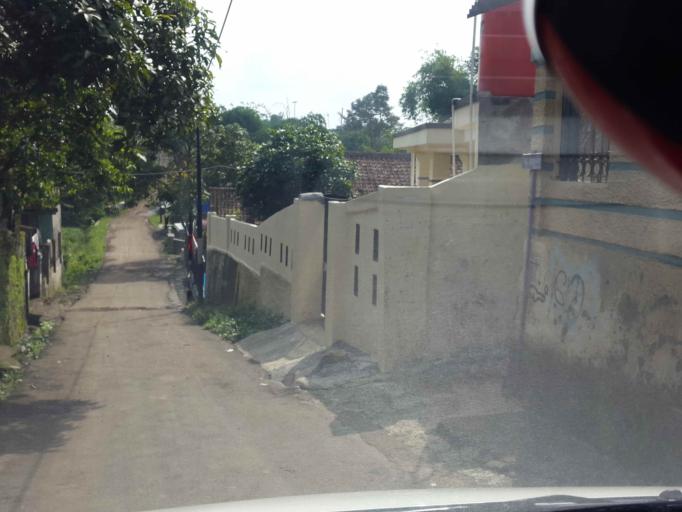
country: ID
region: West Java
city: Sukabumi
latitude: -6.9009
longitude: 106.9656
